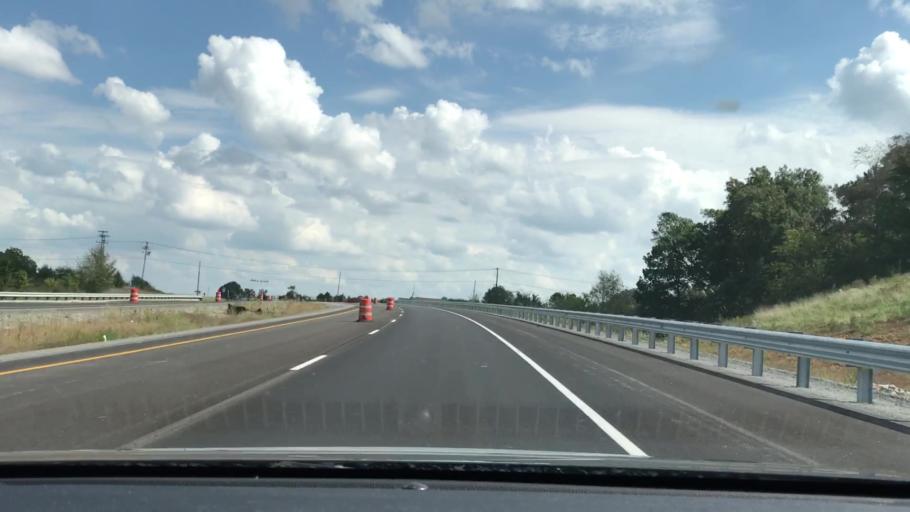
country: US
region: Kentucky
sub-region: Trigg County
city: Cadiz
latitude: 36.8427
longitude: -87.8278
